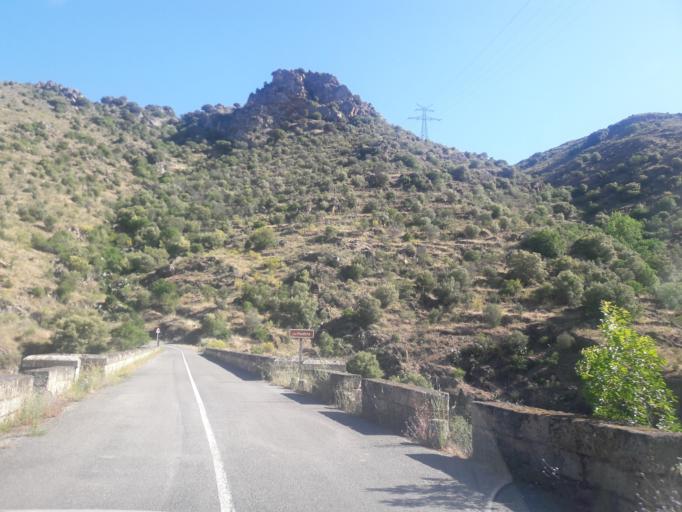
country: ES
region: Castille and Leon
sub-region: Provincia de Salamanca
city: Saucelle
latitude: 41.0295
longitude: -6.7304
